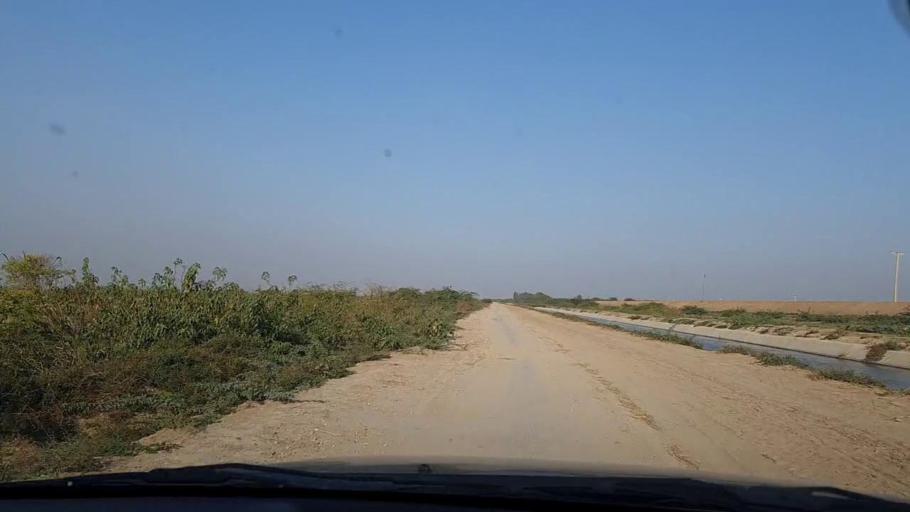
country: PK
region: Sindh
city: Chuhar Jamali
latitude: 24.2838
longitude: 67.7462
